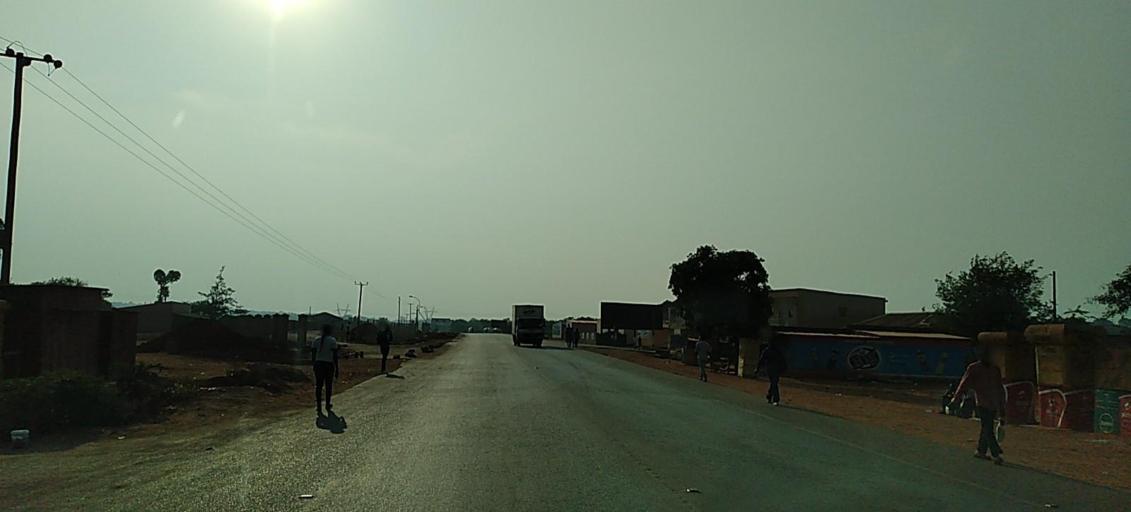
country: ZM
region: North-Western
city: Solwezi
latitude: -12.1928
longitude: 26.4456
